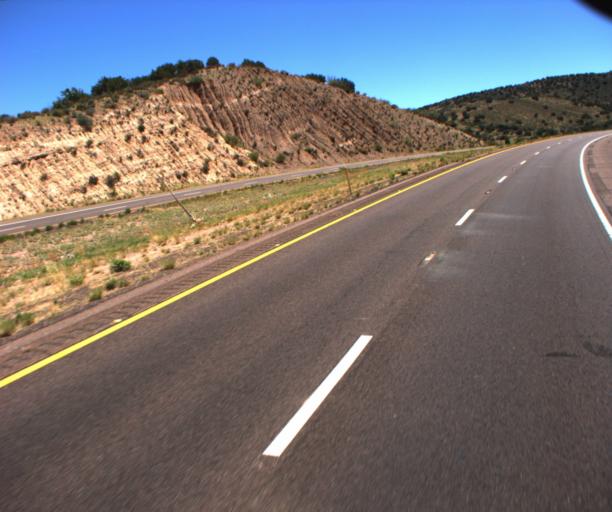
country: US
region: Arizona
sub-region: Gila County
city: Tonto Basin
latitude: 34.0068
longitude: -111.3567
